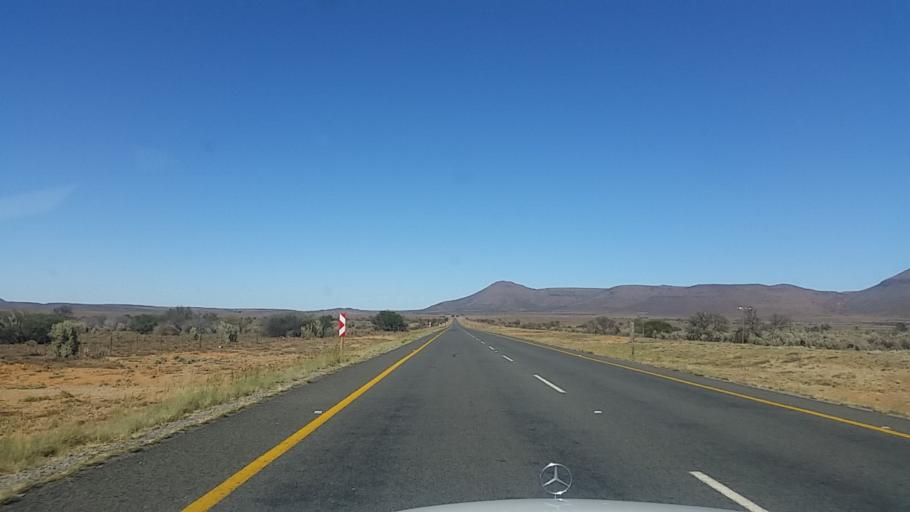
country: ZA
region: Eastern Cape
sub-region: Cacadu District Municipality
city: Graaff-Reinet
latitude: -32.0065
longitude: 24.6583
